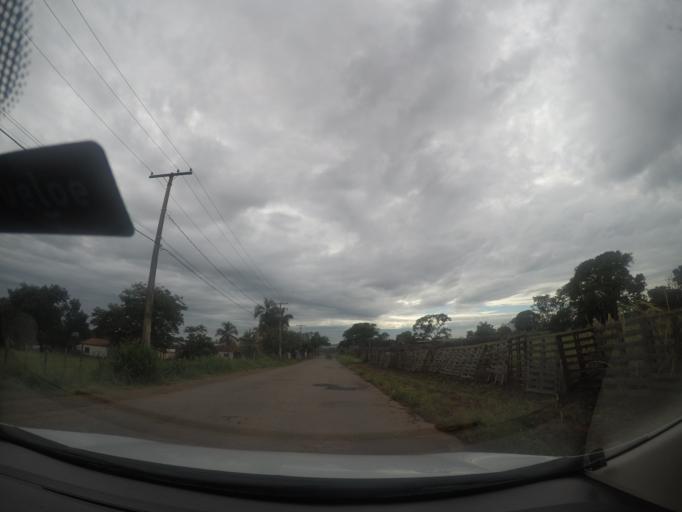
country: BR
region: Goias
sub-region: Goiania
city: Goiania
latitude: -16.6378
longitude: -49.3400
